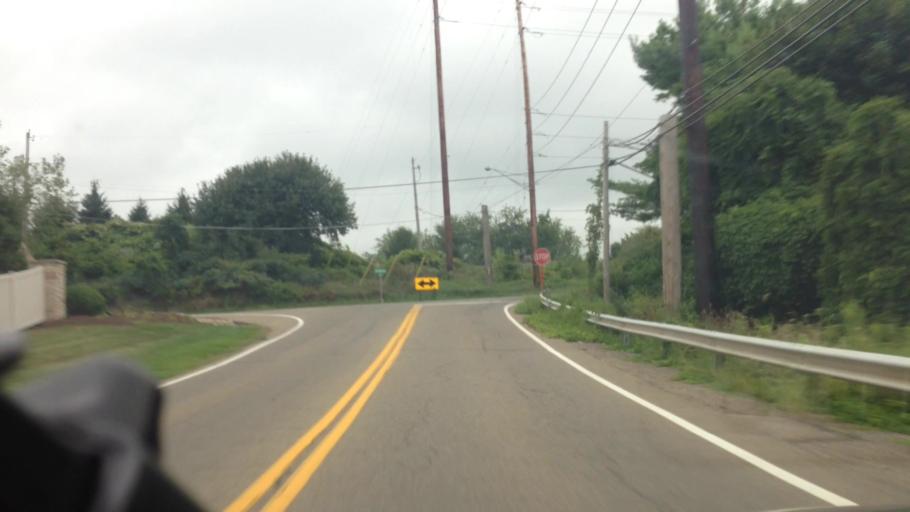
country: US
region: Ohio
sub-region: Stark County
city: Massillon
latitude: 40.8595
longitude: -81.5105
